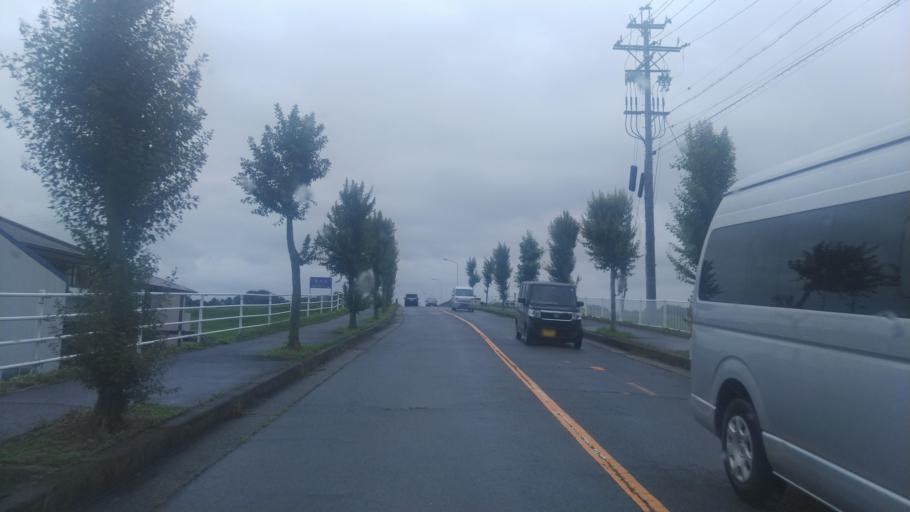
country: JP
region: Aichi
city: Kasugai
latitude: 35.2539
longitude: 137.0193
